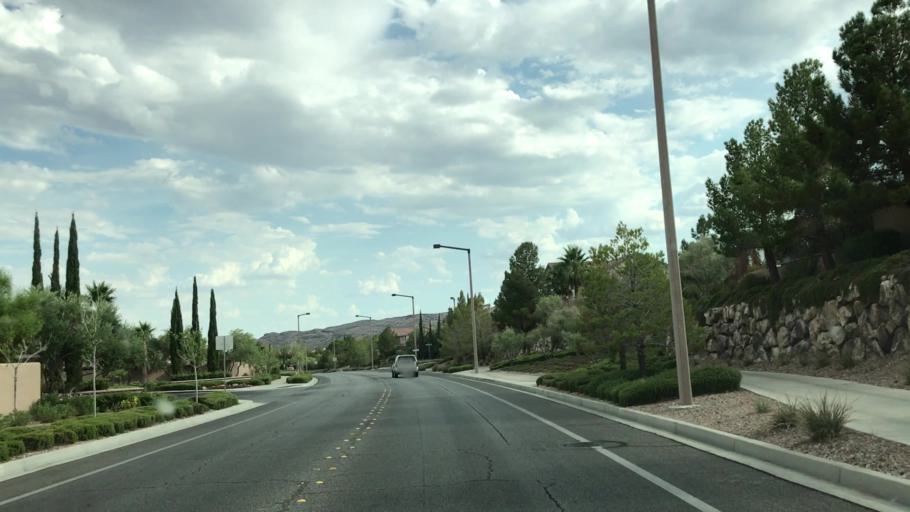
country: US
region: Nevada
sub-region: Clark County
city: Summerlin South
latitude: 36.1748
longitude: -115.3519
